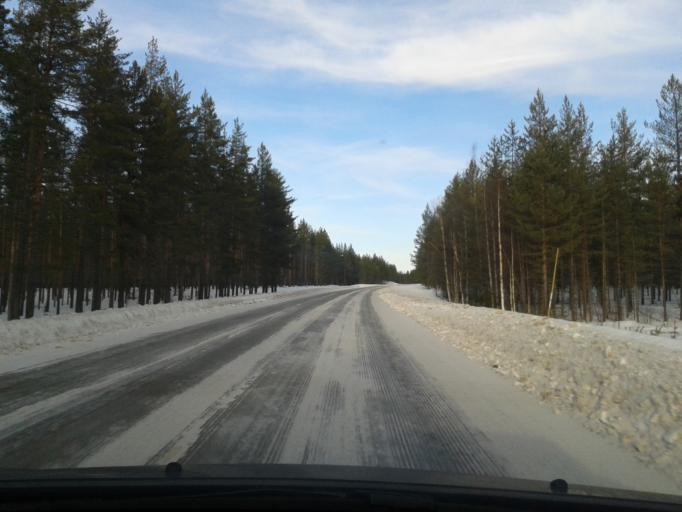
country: SE
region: Vaesternorrland
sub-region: OErnskoeldsviks Kommun
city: Bredbyn
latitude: 63.6110
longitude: 17.9011
